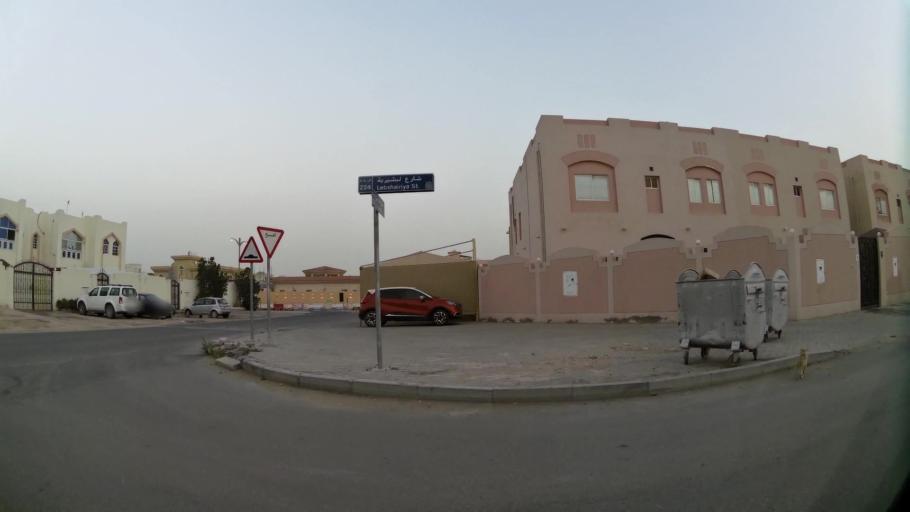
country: QA
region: Baladiyat ar Rayyan
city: Ar Rayyan
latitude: 25.2510
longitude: 51.4650
